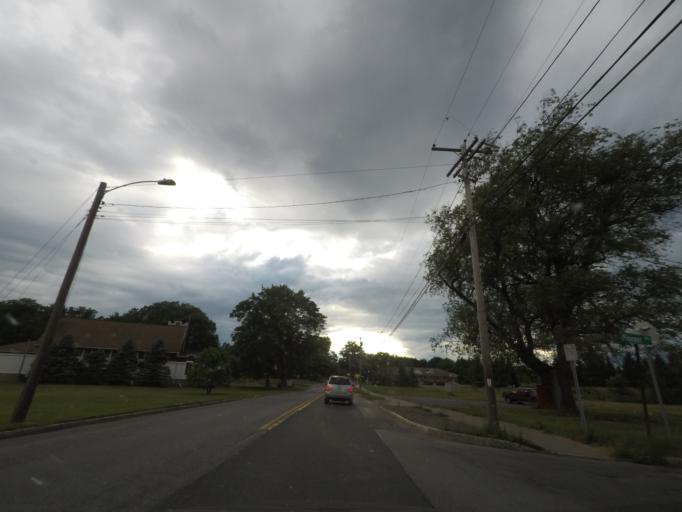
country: US
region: New York
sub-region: Dutchess County
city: Pine Plains
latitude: 41.9803
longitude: -73.6591
